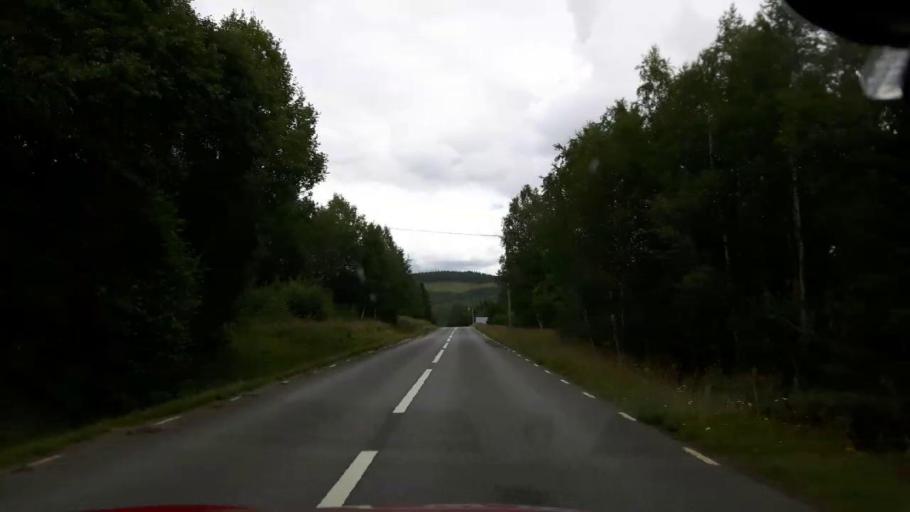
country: NO
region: Nord-Trondelag
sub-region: Lierne
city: Sandvika
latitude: 64.3935
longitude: 14.4818
